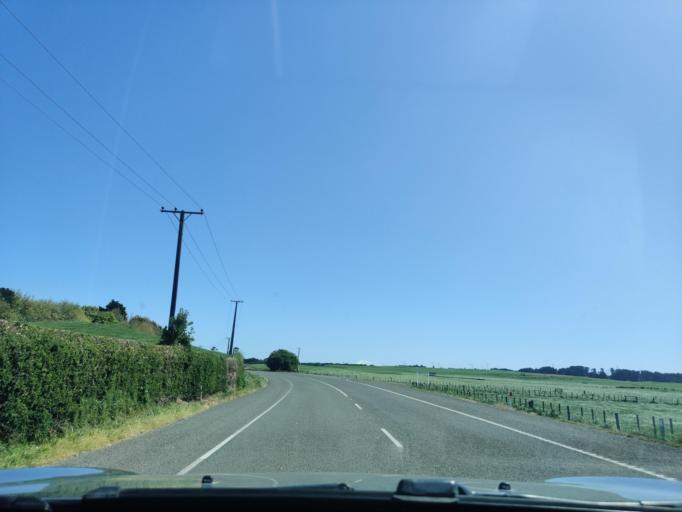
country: NZ
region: Taranaki
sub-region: South Taranaki District
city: Patea
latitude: -39.7788
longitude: 174.6899
